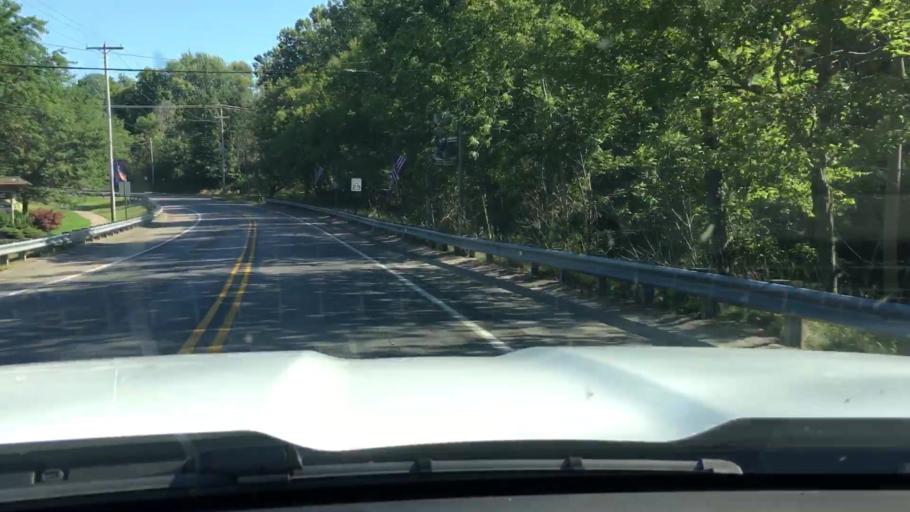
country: US
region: Michigan
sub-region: Muskegon County
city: Ravenna
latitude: 43.1876
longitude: -85.9365
